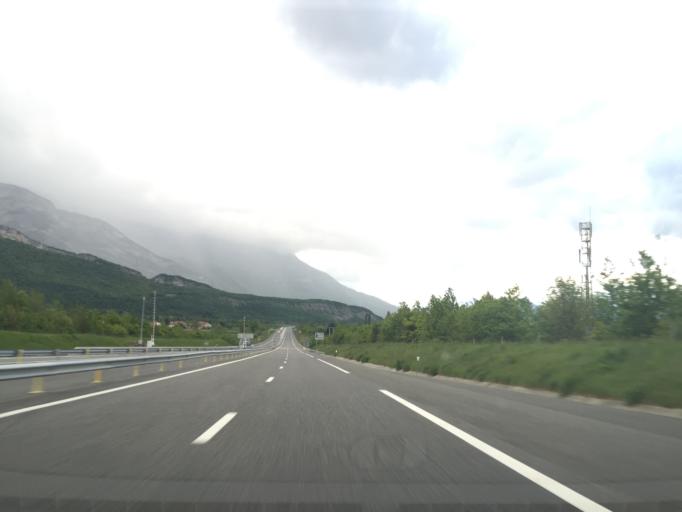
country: FR
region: Rhone-Alpes
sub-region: Departement de l'Isere
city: Vif
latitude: 45.0559
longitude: 5.6862
